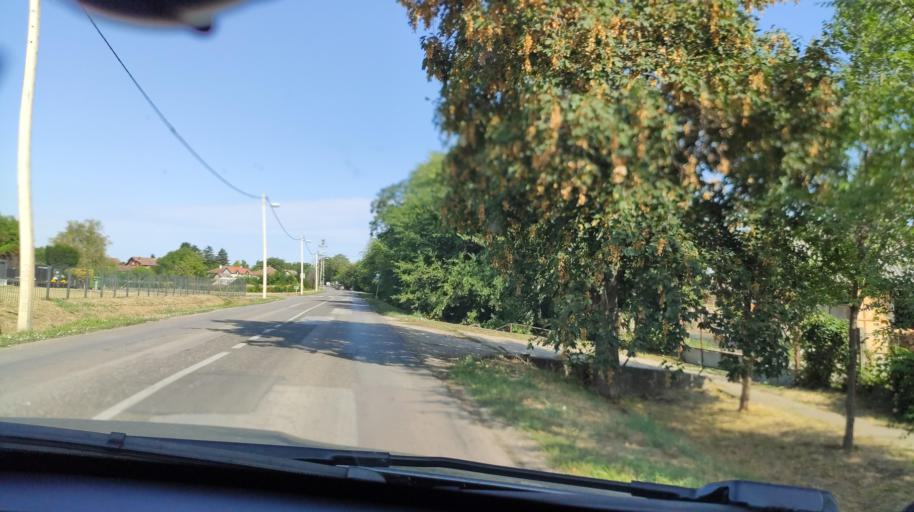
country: RS
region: Autonomna Pokrajina Vojvodina
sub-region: Severnobacki Okrug
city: Backa Topola
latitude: 45.8120
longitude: 19.6221
